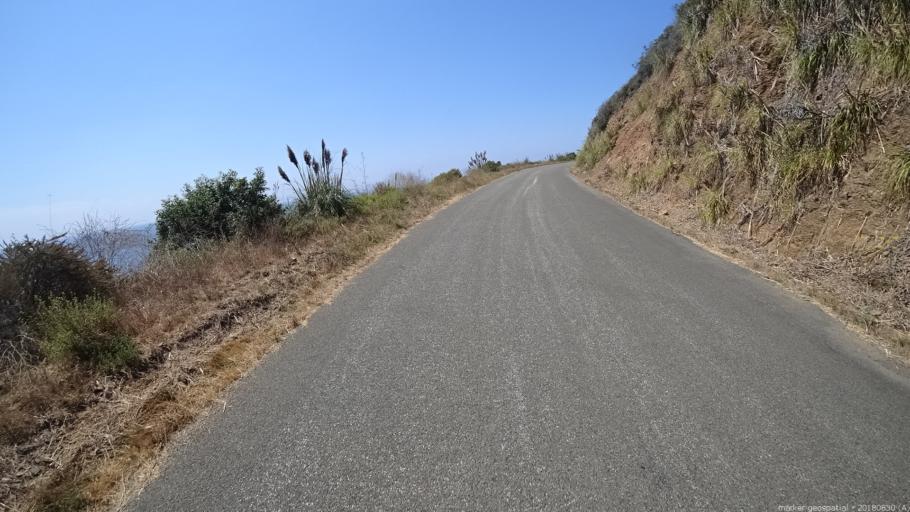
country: US
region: California
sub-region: Monterey County
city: Greenfield
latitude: 35.9847
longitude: -121.4897
